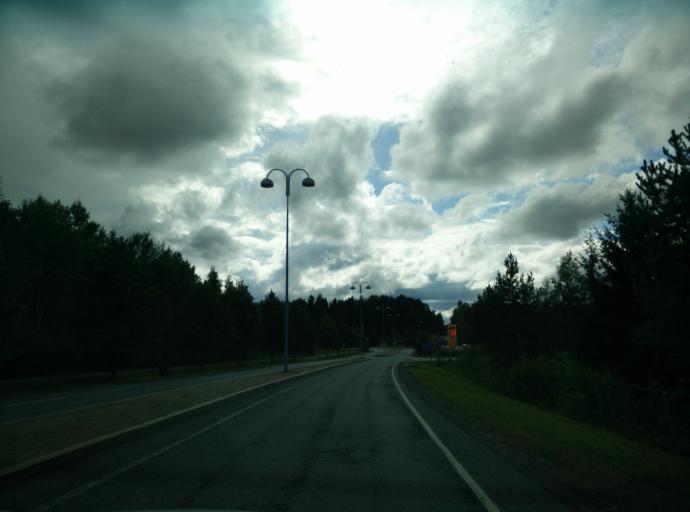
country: FI
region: Haeme
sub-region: Haemeenlinna
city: Kalvola
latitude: 61.0969
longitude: 24.1625
